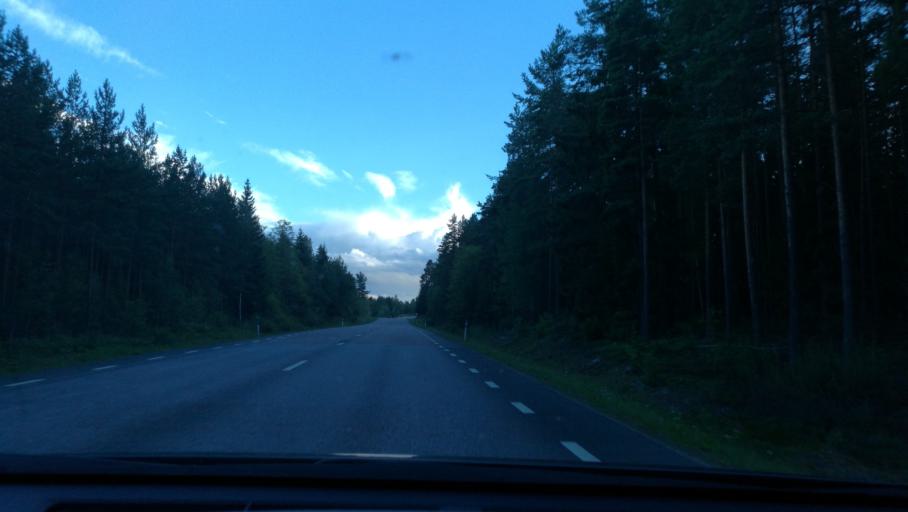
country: SE
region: Soedermanland
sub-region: Katrineholms Kommun
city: Katrineholm
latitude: 59.0481
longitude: 16.2208
